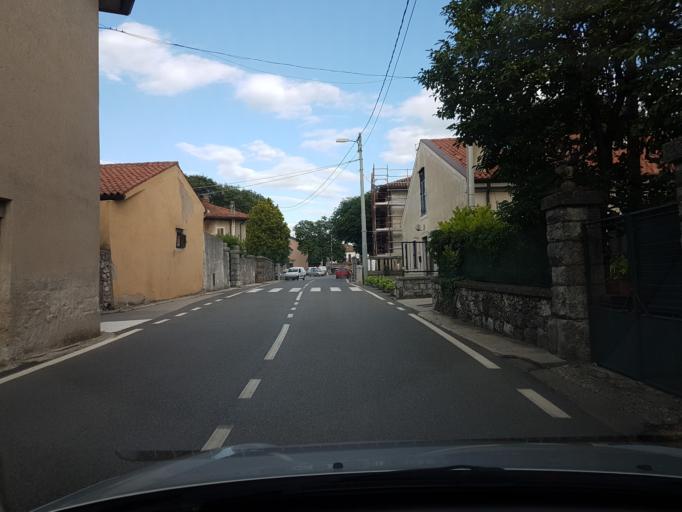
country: IT
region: Friuli Venezia Giulia
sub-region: Provincia di Trieste
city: Villa Opicina
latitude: 45.6730
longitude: 13.8241
